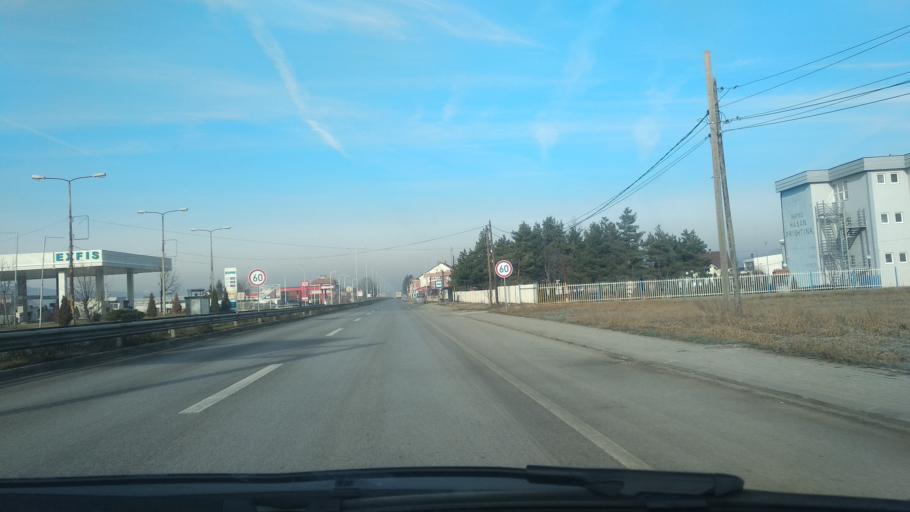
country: XK
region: Pristina
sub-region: Komuna e Obiliqit
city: Obiliq
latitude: 42.7185
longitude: 21.0916
